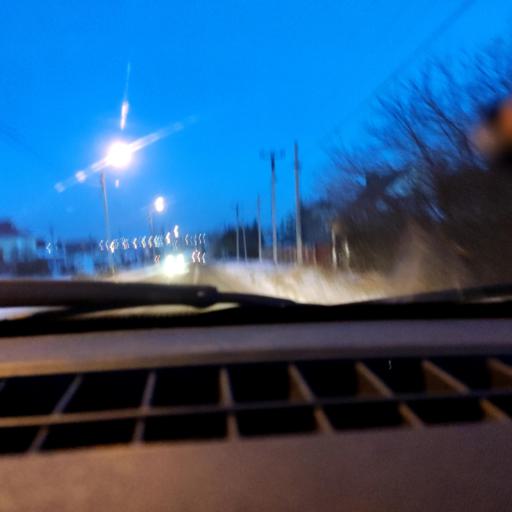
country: RU
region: Bashkortostan
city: Ufa
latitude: 54.6030
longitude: 55.9483
